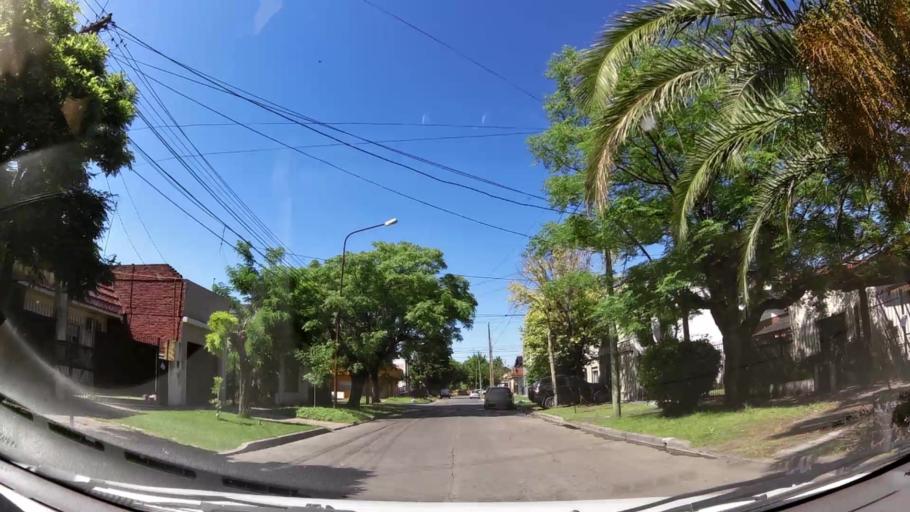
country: AR
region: Buenos Aires
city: Ituzaingo
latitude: -34.6426
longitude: -58.6614
